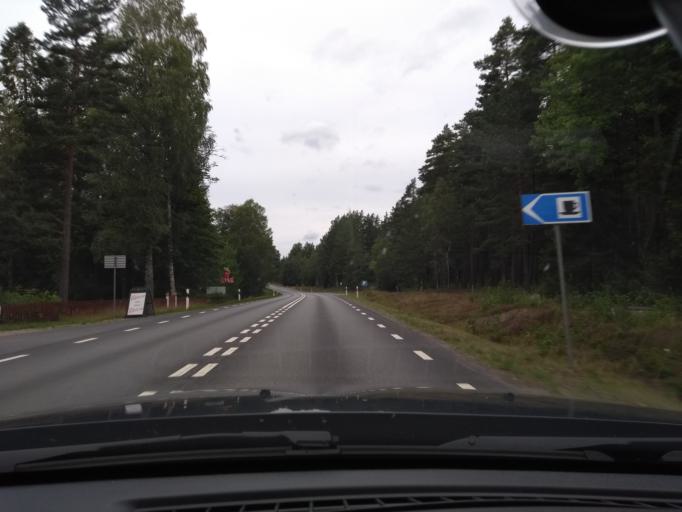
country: SE
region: Joenkoeping
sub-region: Eksjo Kommun
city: Haljarp
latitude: 57.6347
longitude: 15.3325
